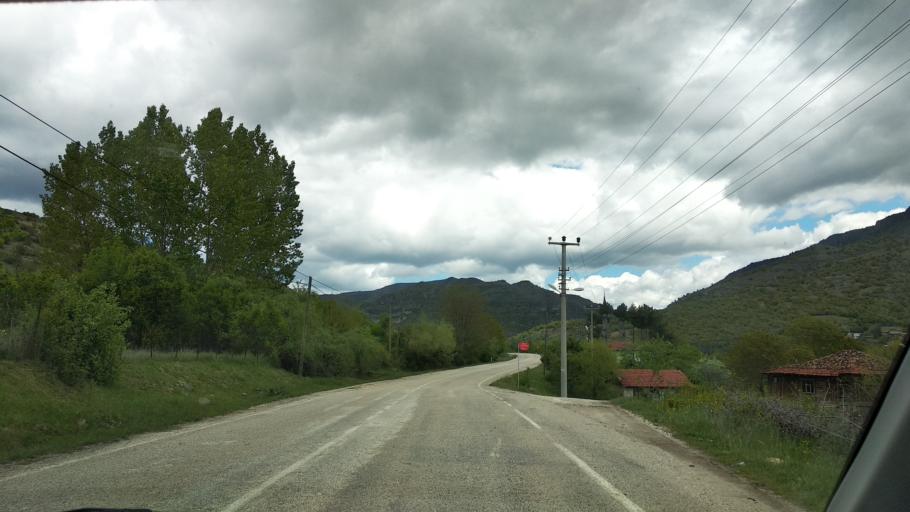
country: TR
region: Bolu
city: Seben
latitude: 40.4182
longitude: 31.5820
